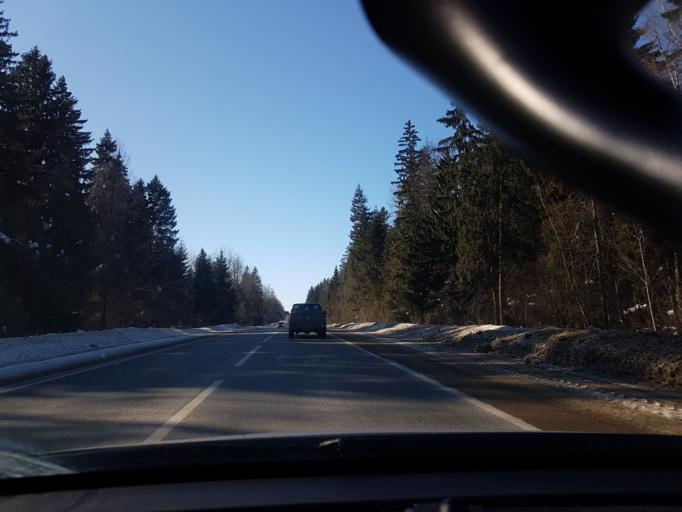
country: RU
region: Moskovskaya
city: Kostrovo
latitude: 55.9135
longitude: 36.7055
